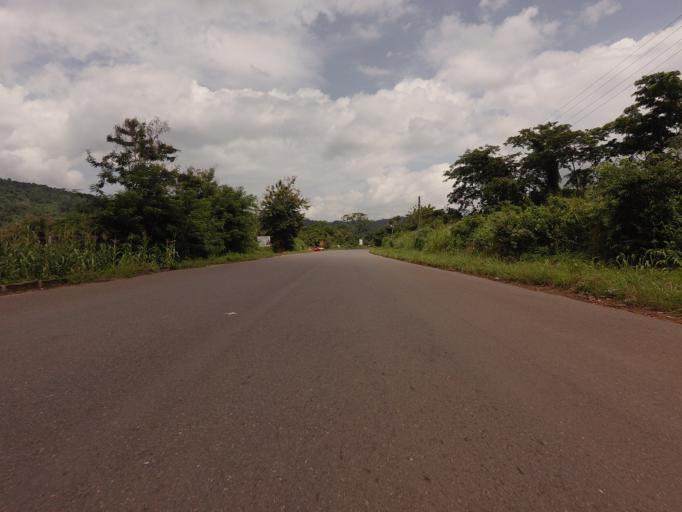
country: GH
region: Volta
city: Ho
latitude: 6.5166
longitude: 0.2190
